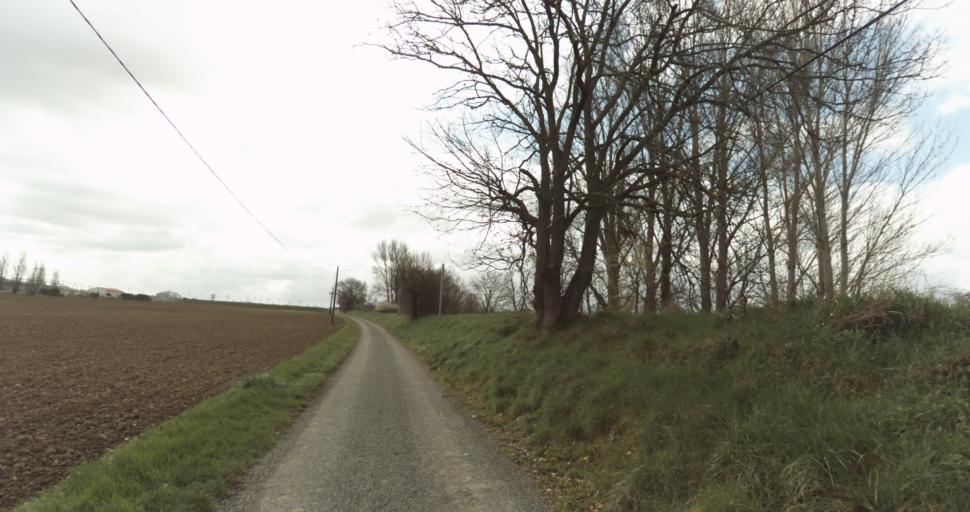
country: FR
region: Midi-Pyrenees
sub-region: Departement de la Haute-Garonne
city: Miremont
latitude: 43.3488
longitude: 1.4419
